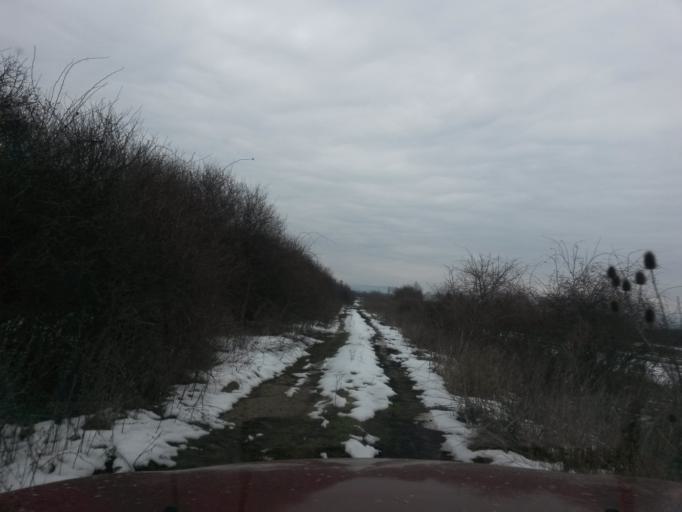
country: SK
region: Kosicky
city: Vinne
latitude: 48.7430
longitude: 22.0241
